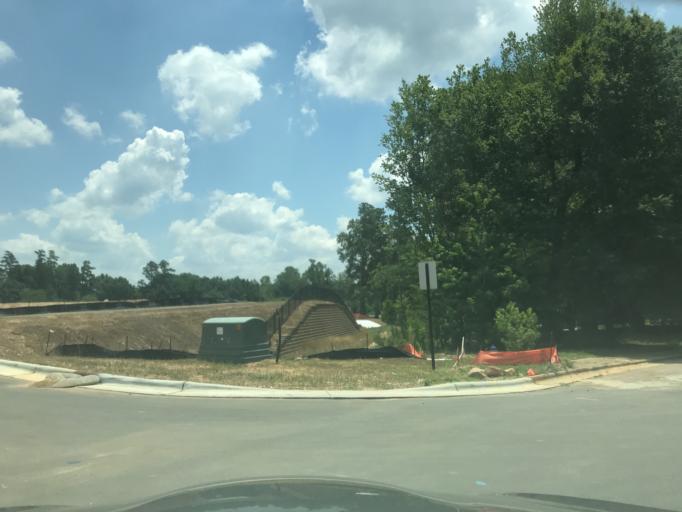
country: US
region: North Carolina
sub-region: Wake County
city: Wake Forest
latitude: 35.9718
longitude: -78.5100
